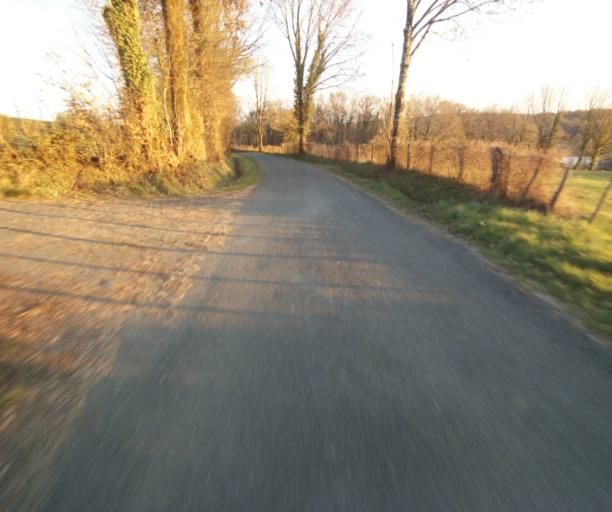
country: FR
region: Limousin
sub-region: Departement de la Correze
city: Uzerche
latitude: 45.3740
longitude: 1.6081
